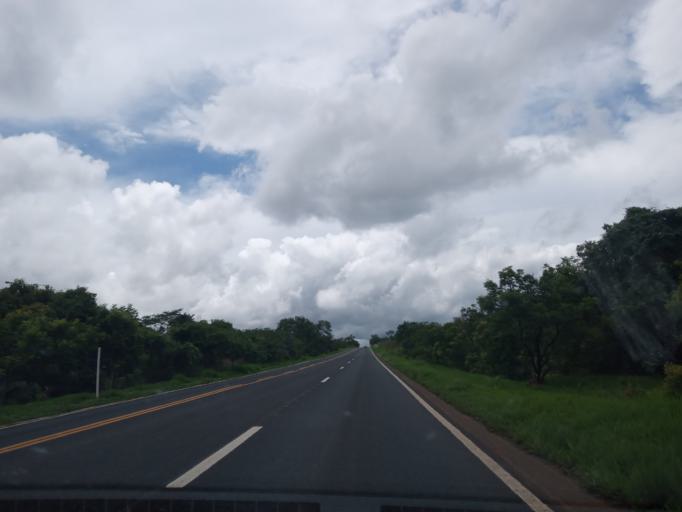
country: BR
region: Minas Gerais
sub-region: Uberaba
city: Uberaba
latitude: -19.2715
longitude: -47.6684
